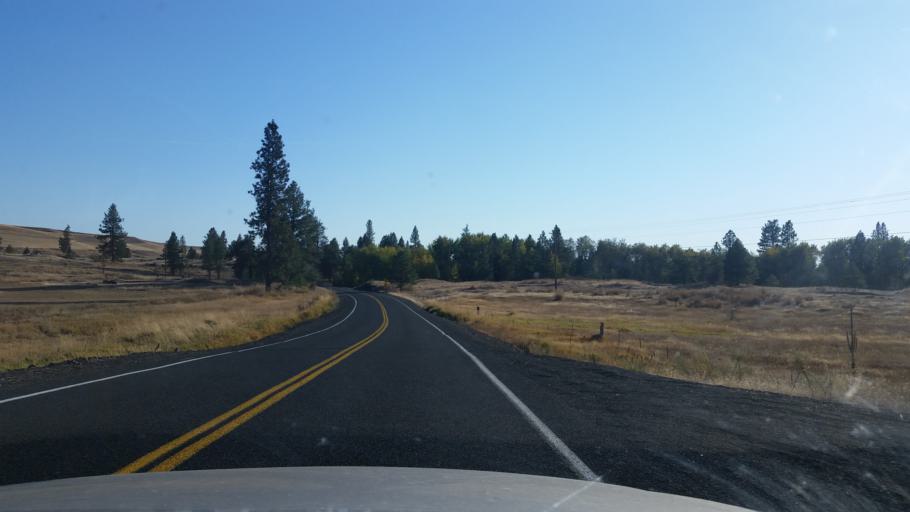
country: US
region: Washington
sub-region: Spokane County
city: Cheney
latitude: 47.3563
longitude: -117.6871
